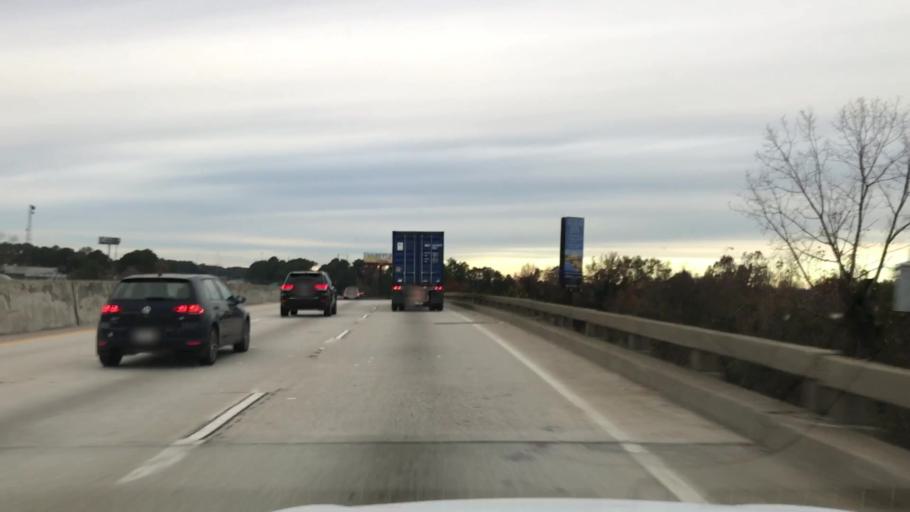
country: US
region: South Carolina
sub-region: Charleston County
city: North Charleston
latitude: 32.8653
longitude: -79.9983
